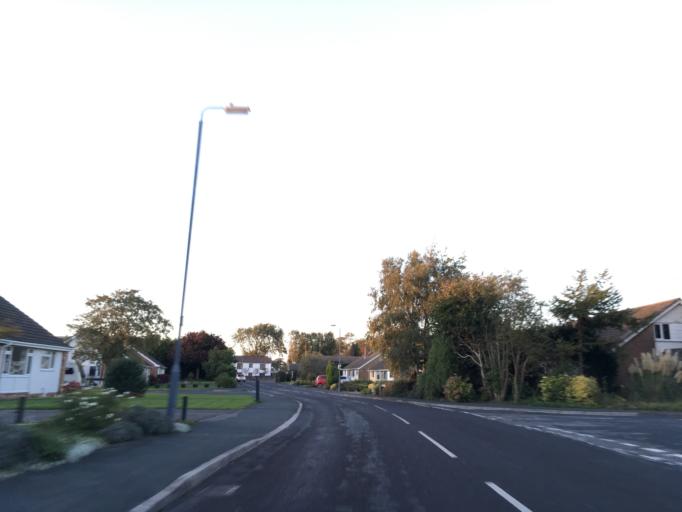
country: GB
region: England
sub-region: South Gloucestershire
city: Alveston
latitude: 51.5912
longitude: -2.5315
